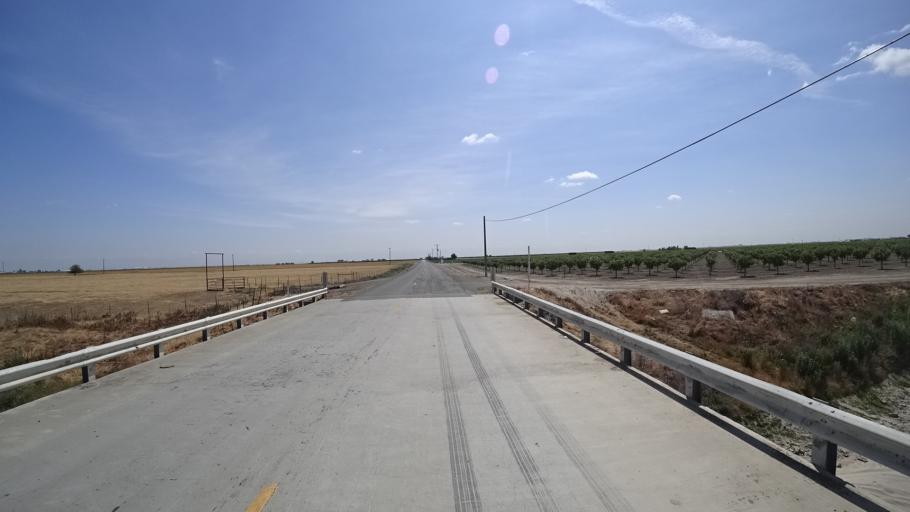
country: US
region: California
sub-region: Kings County
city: Home Garden
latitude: 36.2695
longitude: -119.5543
